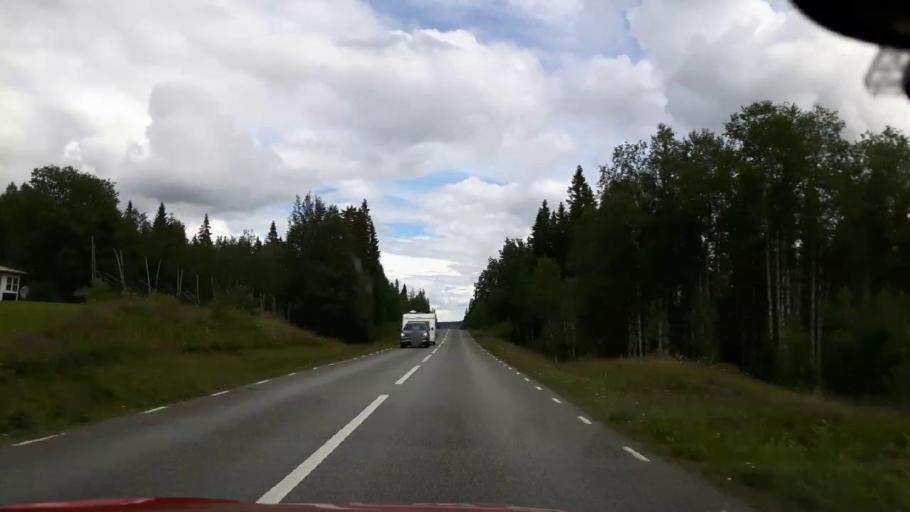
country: NO
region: Nord-Trondelag
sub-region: Lierne
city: Sandvika
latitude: 64.3900
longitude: 14.4448
